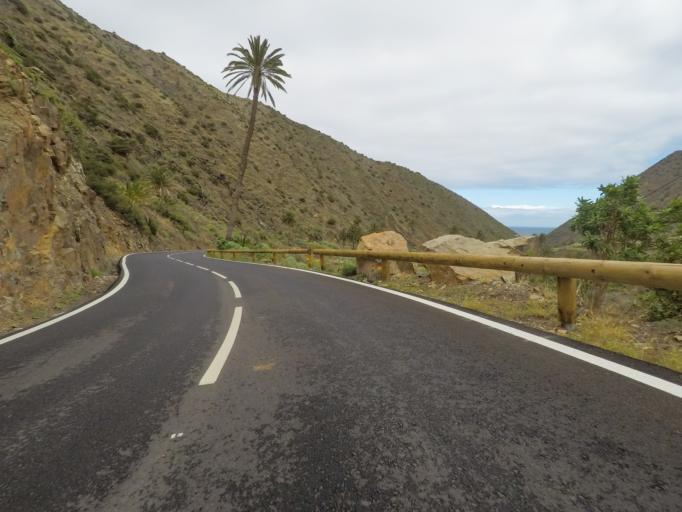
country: ES
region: Canary Islands
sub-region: Provincia de Santa Cruz de Tenerife
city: Vallehermosa
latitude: 28.1913
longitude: -17.2616
